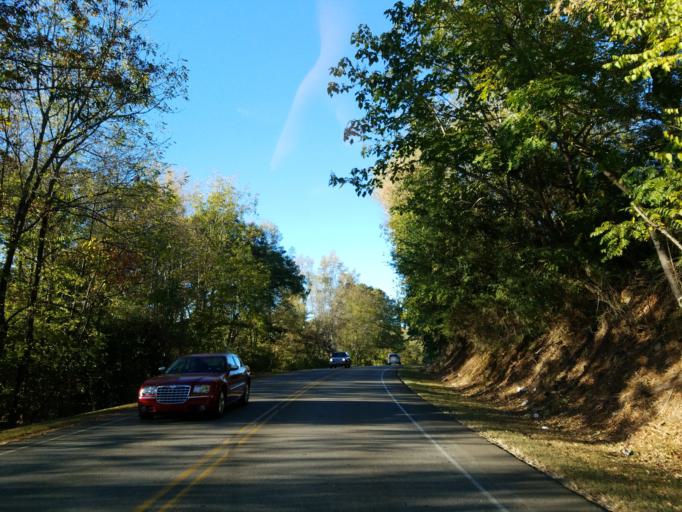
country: US
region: Georgia
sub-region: Pickens County
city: Nelson
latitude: 34.3806
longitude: -84.3744
